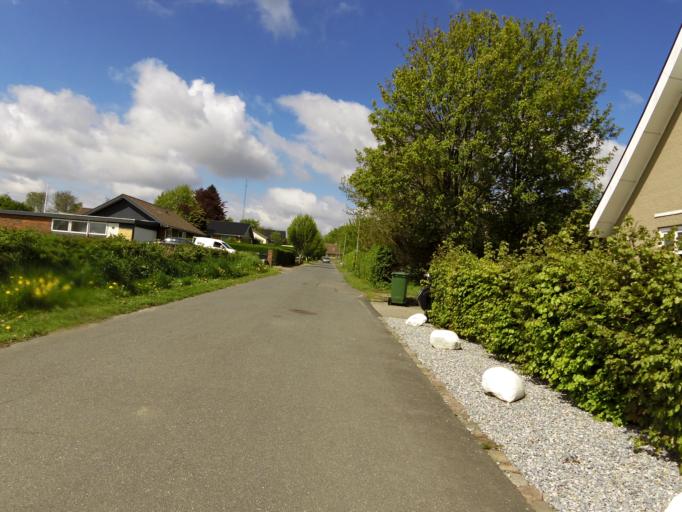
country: DK
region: South Denmark
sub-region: Vejen Kommune
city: Rodding
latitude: 55.3286
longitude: 9.0602
